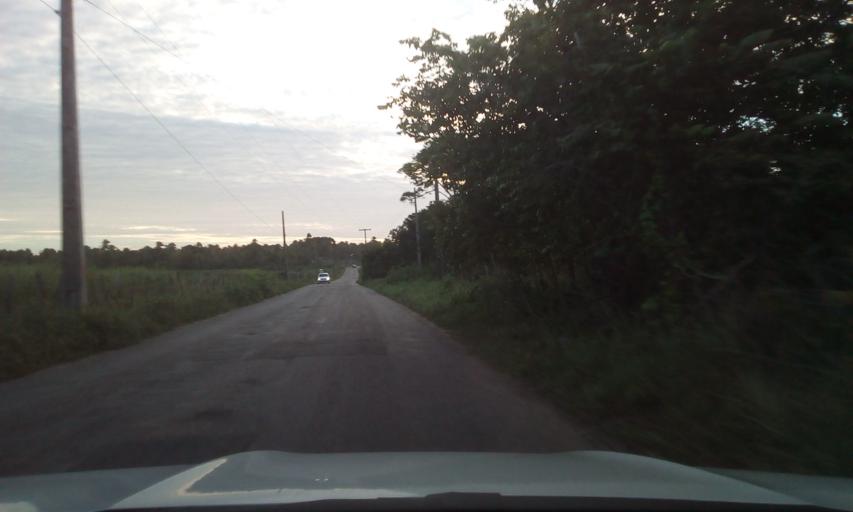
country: BR
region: Paraiba
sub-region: Conde
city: Conde
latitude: -7.2217
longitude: -34.8288
